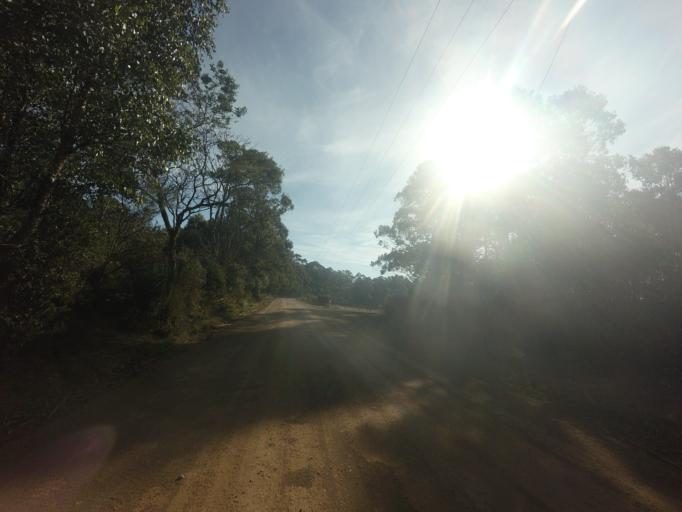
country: AU
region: Tasmania
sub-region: Sorell
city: Sorell
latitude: -42.5045
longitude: 147.5461
